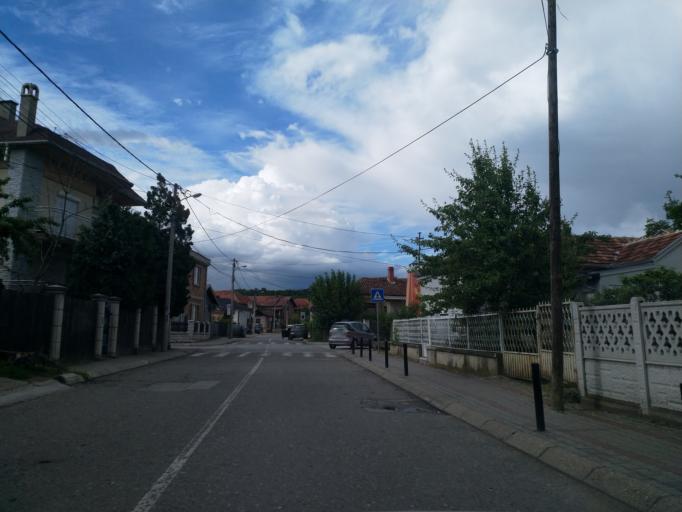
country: RS
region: Central Serbia
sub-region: Pomoravski Okrug
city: Paracin
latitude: 43.8650
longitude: 21.4130
